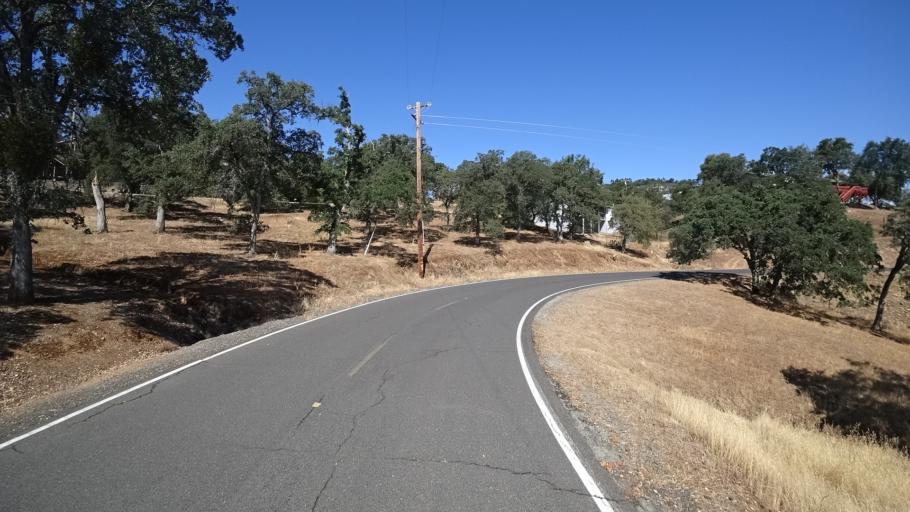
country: US
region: California
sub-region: Calaveras County
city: Copperopolis
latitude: 37.9264
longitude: -120.6289
